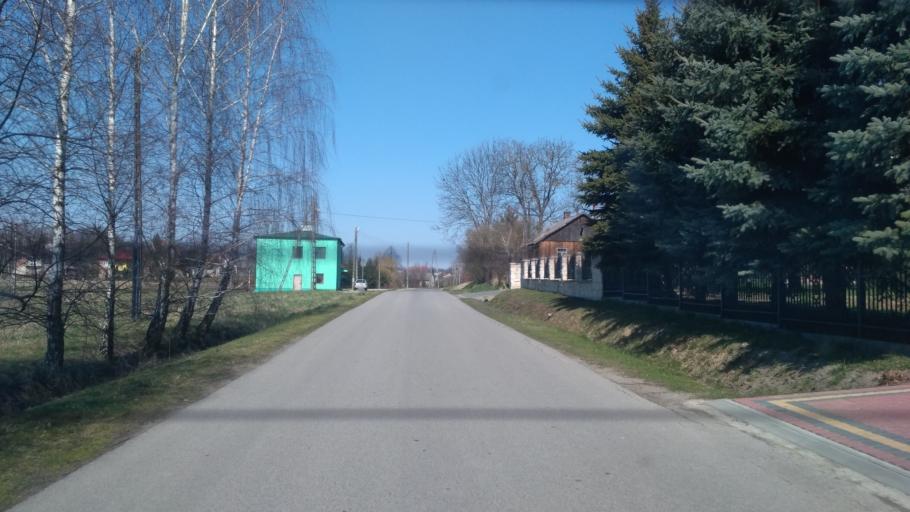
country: PL
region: Subcarpathian Voivodeship
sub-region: Powiat jaroslawski
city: Pawlosiow
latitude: 49.9604
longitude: 22.6507
